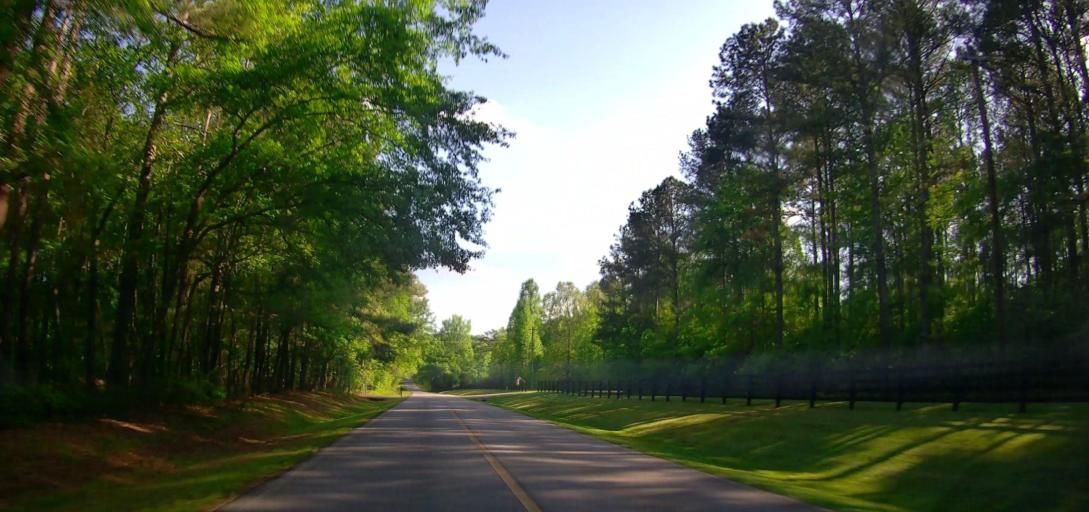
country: US
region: Georgia
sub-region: Morgan County
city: Madison
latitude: 33.5312
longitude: -83.4789
